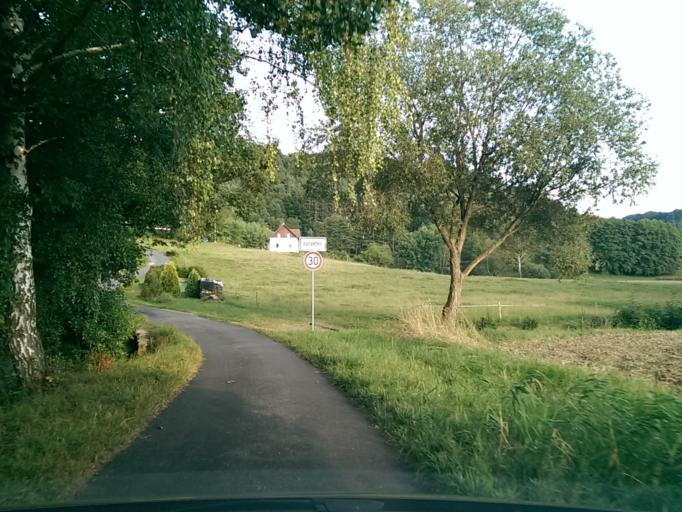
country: CZ
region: Liberecky
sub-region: Okres Semily
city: Turnov
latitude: 50.5456
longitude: 15.1270
